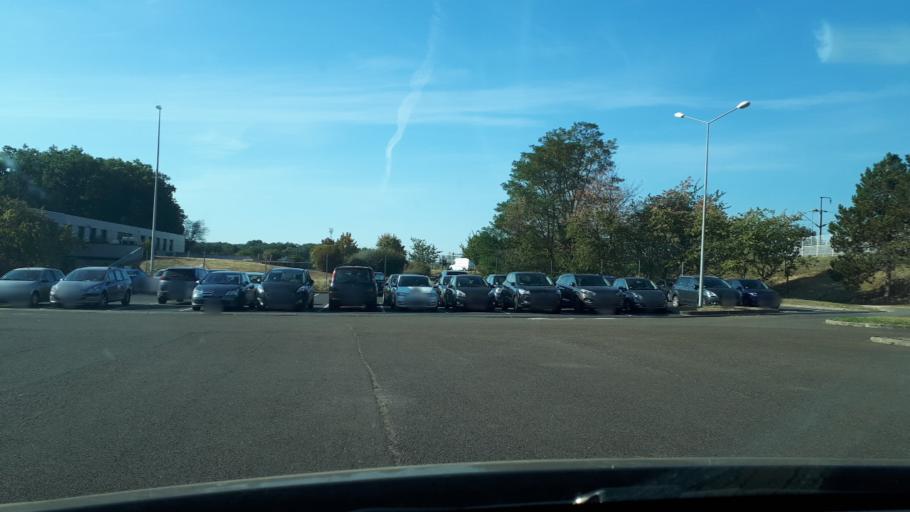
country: FR
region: Centre
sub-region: Departement du Loir-et-Cher
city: Naveil
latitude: 47.8215
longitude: 1.0213
